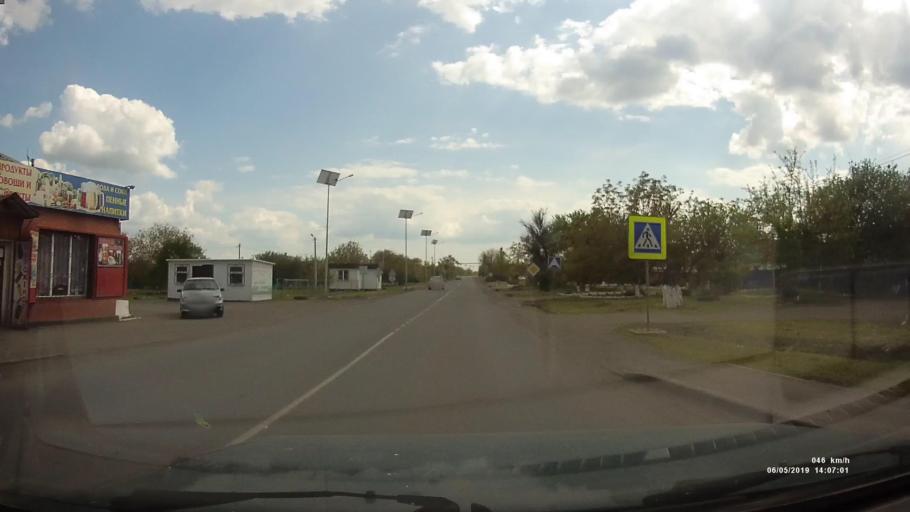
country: RU
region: Rostov
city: Shakhty
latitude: 47.6844
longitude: 40.3027
